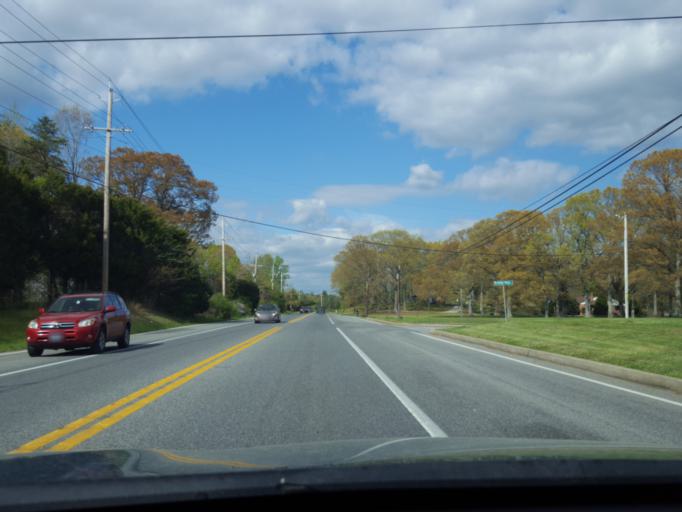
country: US
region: Maryland
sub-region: Charles County
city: Hughesville
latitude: 38.5373
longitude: -76.7695
